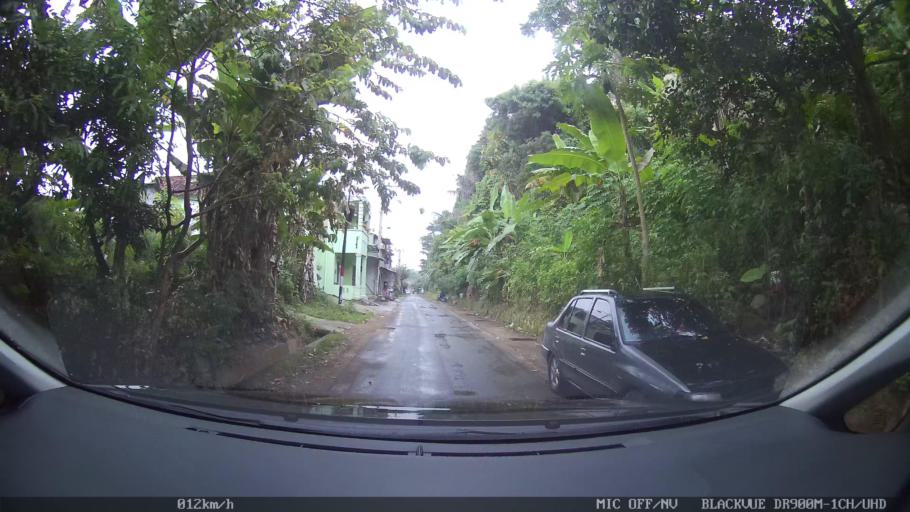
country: ID
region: Lampung
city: Bandarlampung
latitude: -5.4370
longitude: 105.2811
